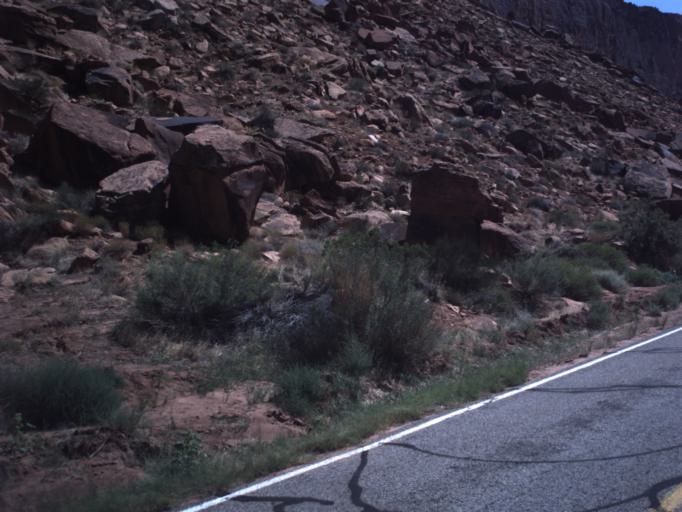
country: US
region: Utah
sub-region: Grand County
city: Moab
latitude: 38.7963
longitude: -109.3398
